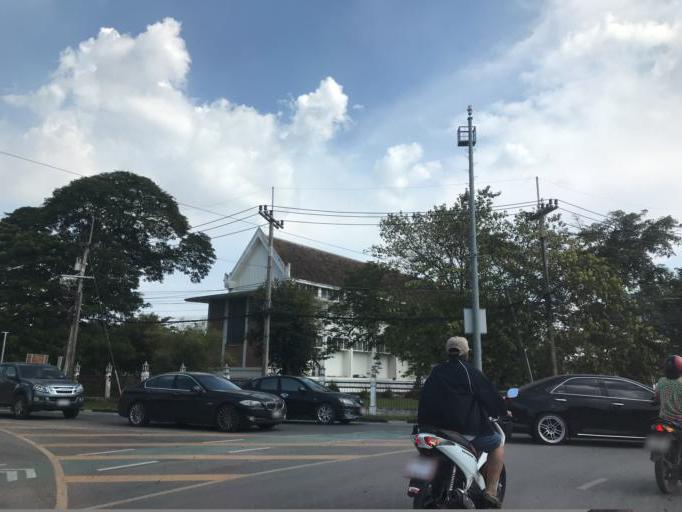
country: TH
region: Phra Nakhon Si Ayutthaya
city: Phra Nakhon Si Ayutthaya
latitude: 14.3524
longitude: 100.5607
